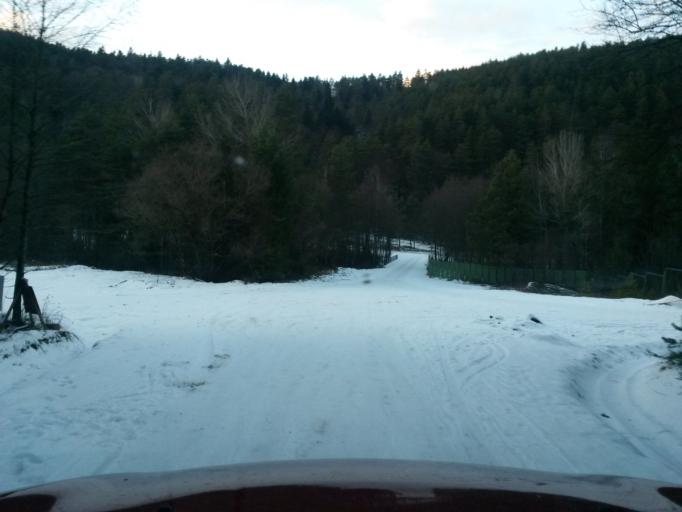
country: SK
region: Kosicky
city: Medzev
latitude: 48.7821
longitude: 20.7966
